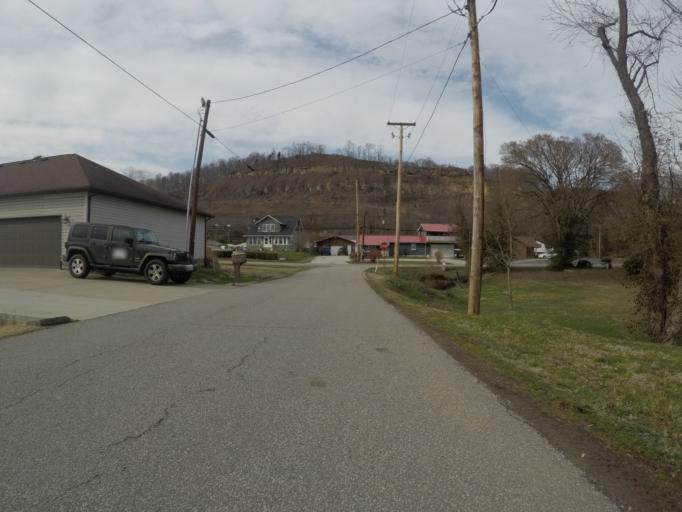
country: US
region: West Virginia
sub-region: Cabell County
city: Huntington
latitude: 38.4224
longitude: -82.4803
